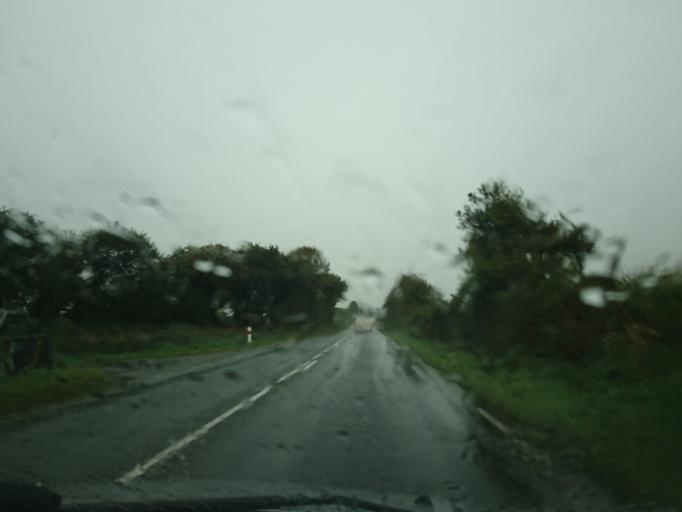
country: FR
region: Brittany
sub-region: Departement du Finistere
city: Gouesnou
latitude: 48.4714
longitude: -4.4425
